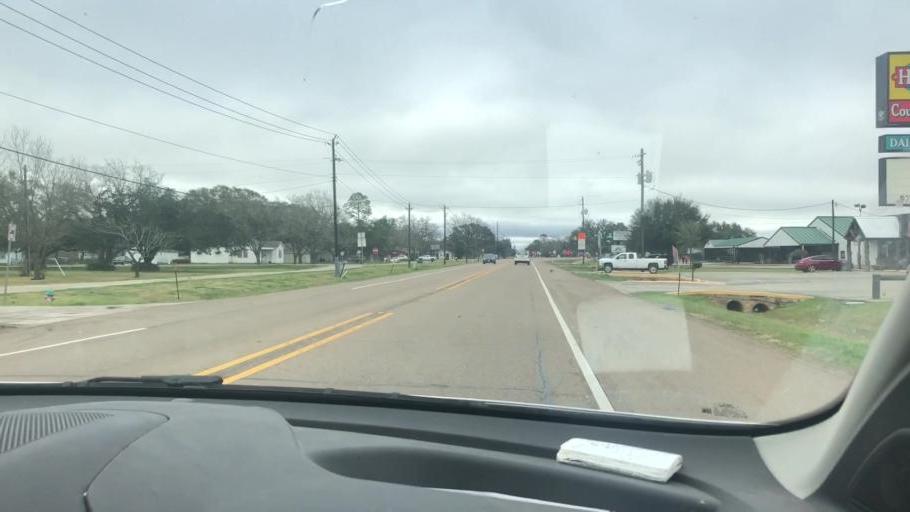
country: US
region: Texas
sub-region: Wharton County
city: Wharton
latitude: 29.3072
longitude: -96.0865
